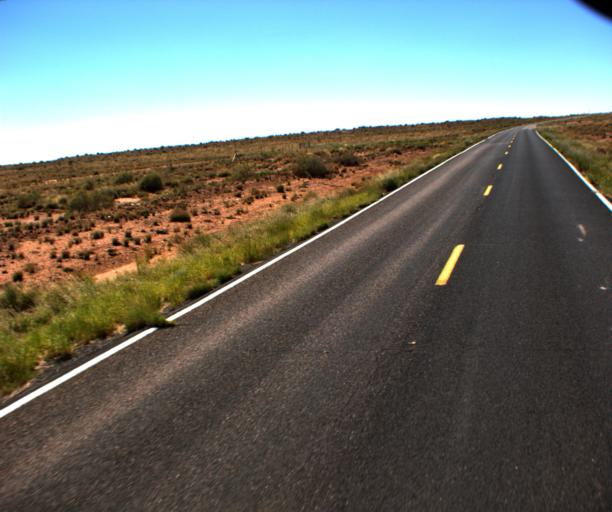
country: US
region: Arizona
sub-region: Coconino County
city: LeChee
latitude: 35.1297
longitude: -110.8783
